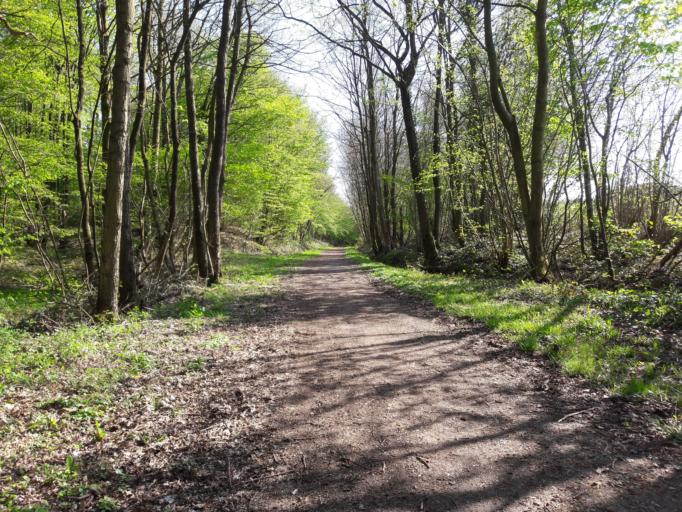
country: FR
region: Nord-Pas-de-Calais
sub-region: Departement du Nord
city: Sains-du-Nord
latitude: 50.1454
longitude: 4.0682
